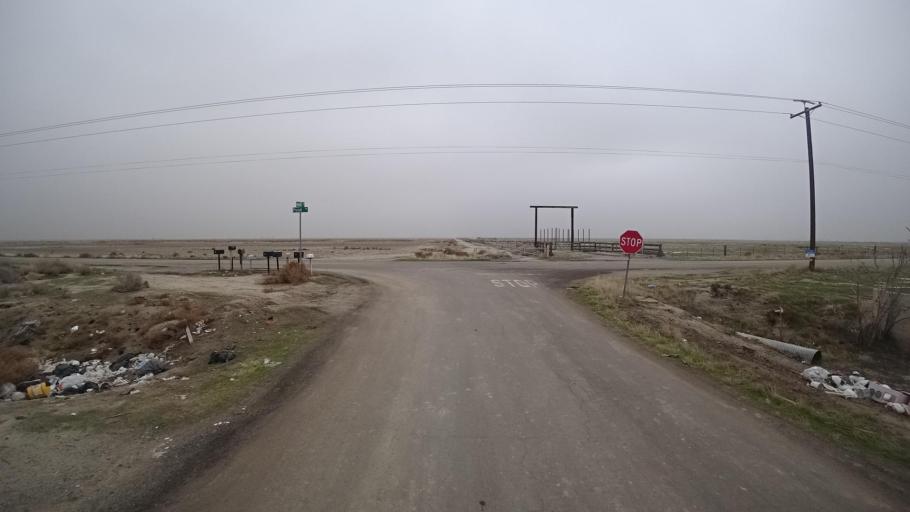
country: US
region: California
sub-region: Tulare County
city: Alpaugh
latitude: 35.7177
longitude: -119.4727
